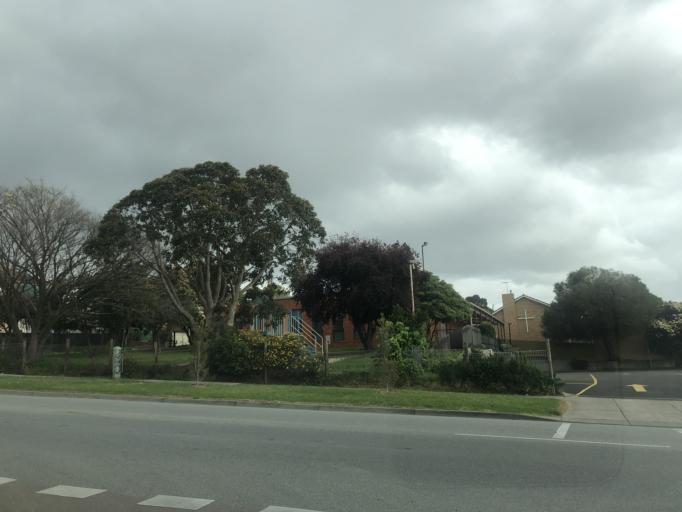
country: AU
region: Victoria
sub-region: Casey
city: Doveton
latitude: -37.9871
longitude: 145.2354
